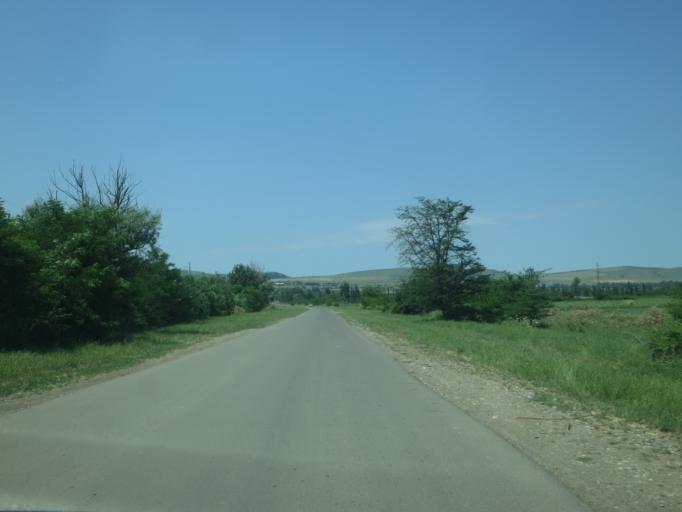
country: GE
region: Kakheti
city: Sagarejo
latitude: 41.6661
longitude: 45.3847
